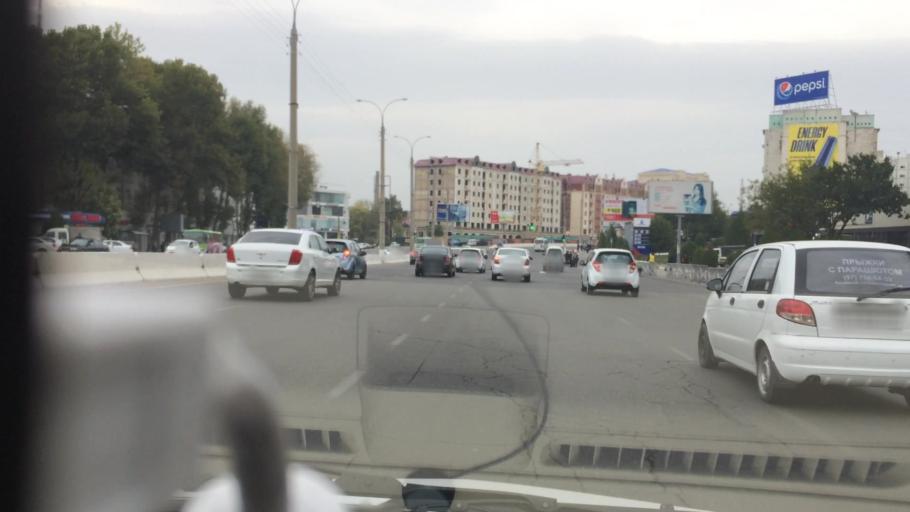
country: UZ
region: Toshkent
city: Salor
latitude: 41.3148
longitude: 69.3264
